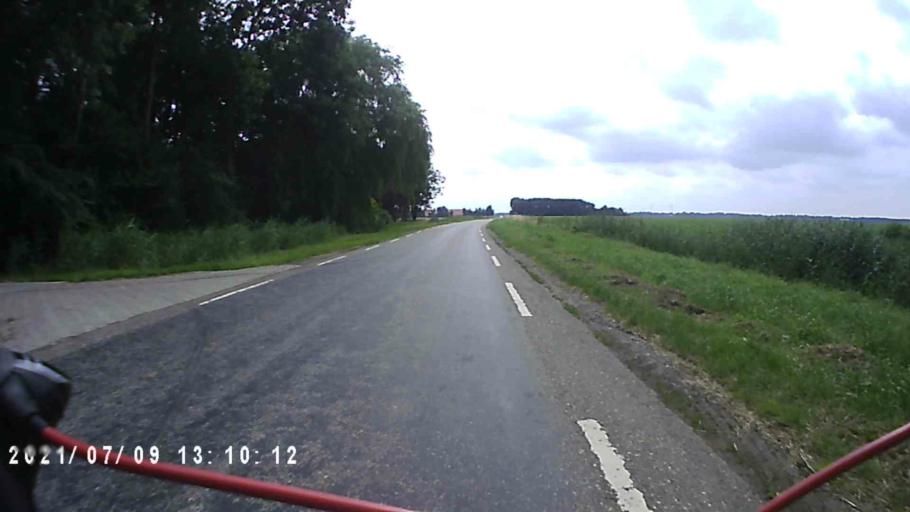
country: NL
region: Groningen
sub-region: Gemeente  Oldambt
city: Winschoten
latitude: 53.1282
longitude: 7.1226
